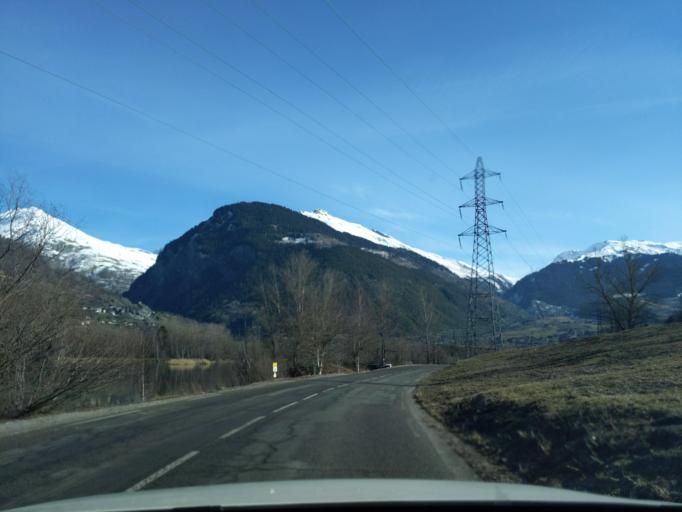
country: FR
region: Rhone-Alpes
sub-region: Departement de la Savoie
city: Bourg-Saint-Maurice
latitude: 45.6141
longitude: 6.7775
